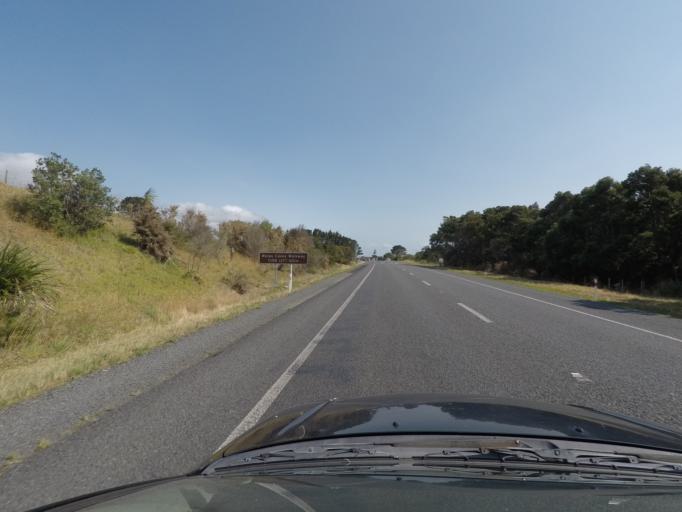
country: NZ
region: Northland
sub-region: Whangarei
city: Ruakaka
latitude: -35.9381
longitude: 174.4560
